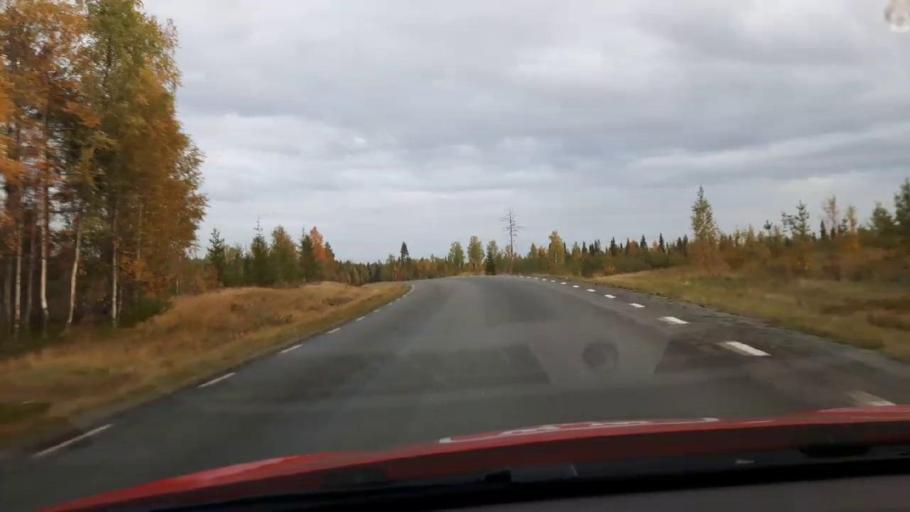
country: SE
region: Jaemtland
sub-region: OEstersunds Kommun
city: Lit
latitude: 63.3161
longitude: 15.0923
